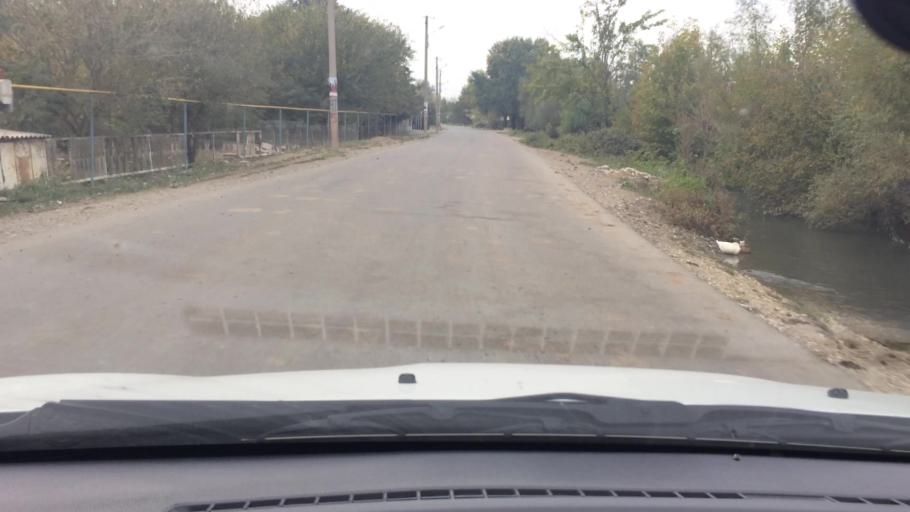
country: AM
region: Tavush
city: Berdavan
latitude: 41.3494
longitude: 44.9736
